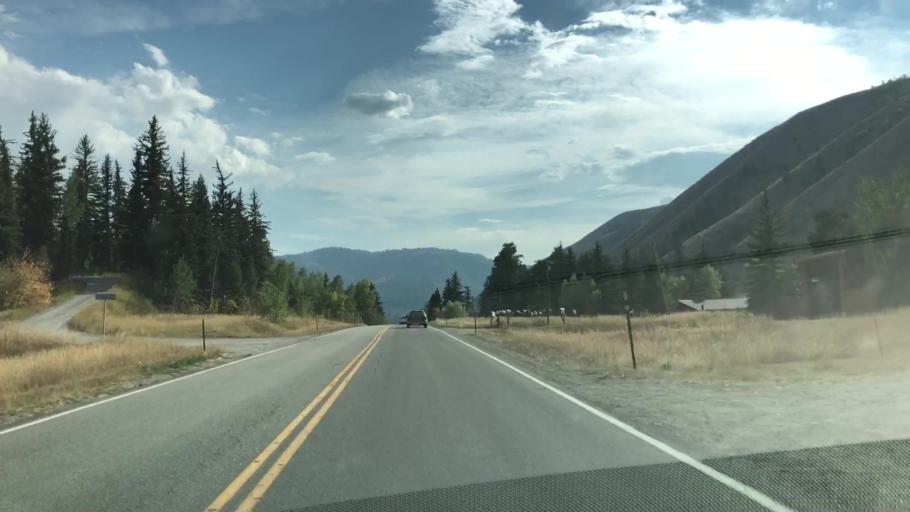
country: US
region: Wyoming
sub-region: Teton County
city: Hoback
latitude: 43.3395
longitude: -110.7236
